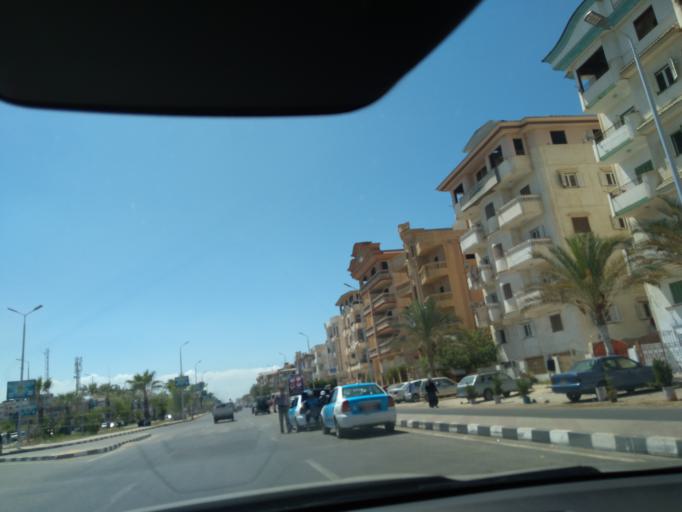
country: EG
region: Dumyat
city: Faraskur
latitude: 31.4423
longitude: 31.6857
